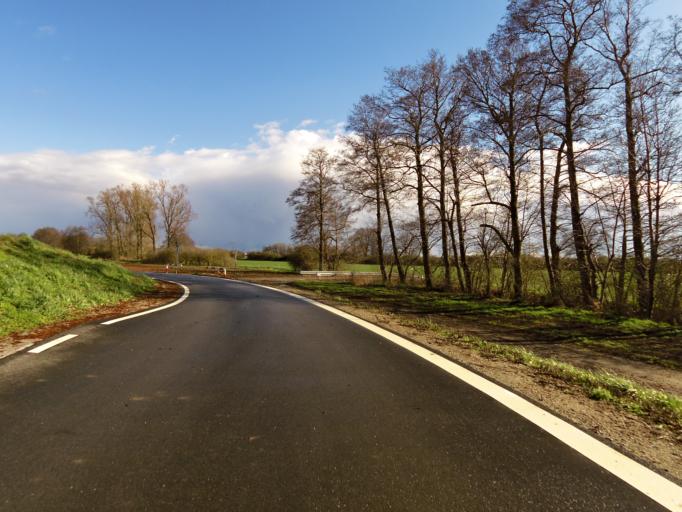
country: DE
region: Hesse
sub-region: Regierungsbezirk Darmstadt
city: Biblis
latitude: 49.6771
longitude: 8.4228
